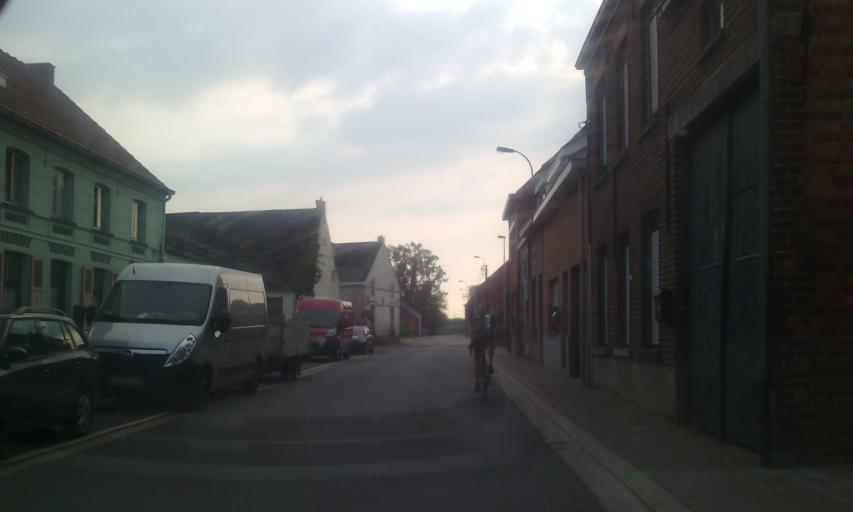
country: BE
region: Flanders
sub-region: Provincie Oost-Vlaanderen
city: Lede
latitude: 50.9625
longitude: 4.0100
